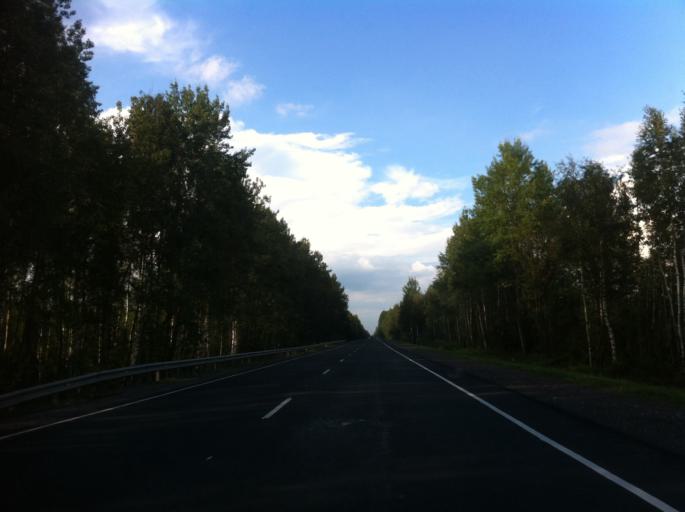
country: RU
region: Leningrad
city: Luga
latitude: 58.4571
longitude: 29.7616
